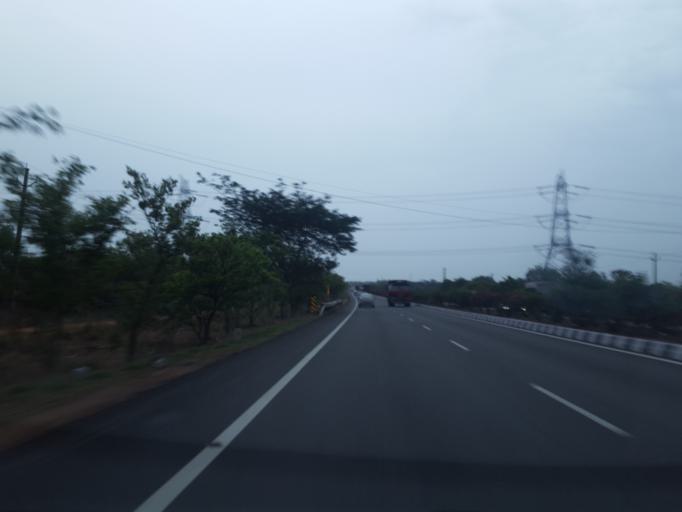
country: IN
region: Telangana
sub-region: Mahbubnagar
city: Farrukhnagar
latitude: 17.0845
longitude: 78.2337
